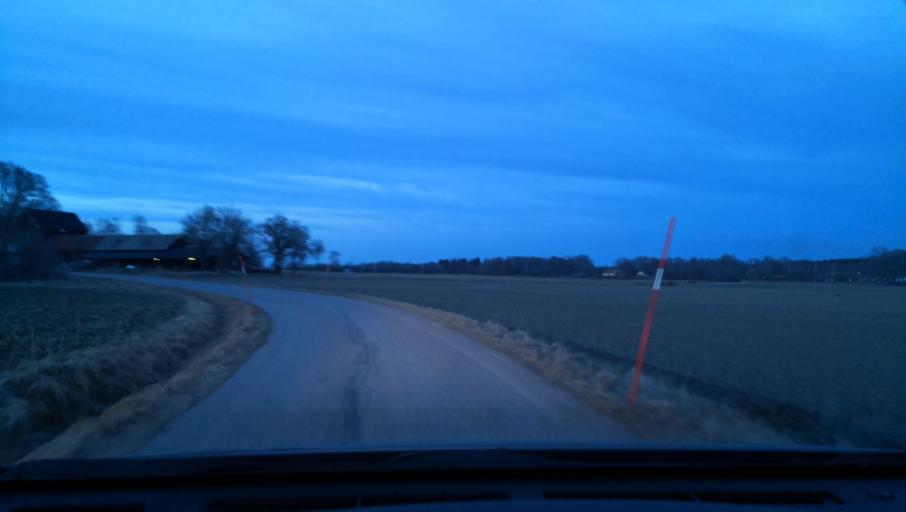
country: SE
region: Uppsala
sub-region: Enkopings Kommun
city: Dalby
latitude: 59.5469
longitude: 17.3670
